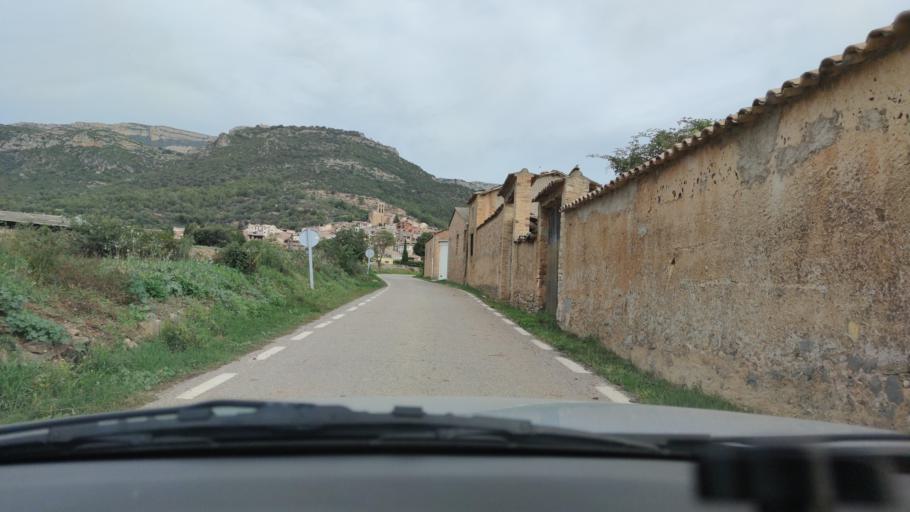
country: ES
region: Catalonia
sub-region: Provincia de Lleida
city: Artesa de Segre
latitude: 41.9904
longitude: 1.0234
